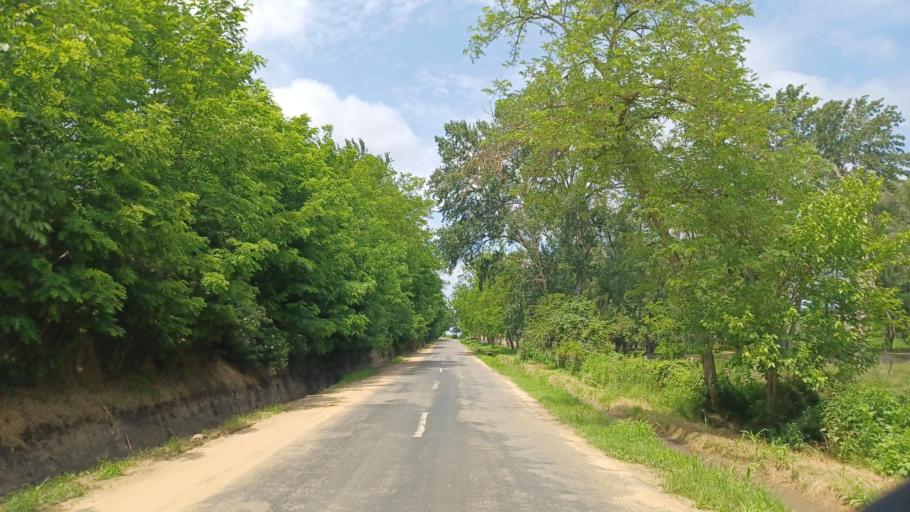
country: HU
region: Tolna
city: Simontornya
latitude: 46.6966
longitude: 18.5177
